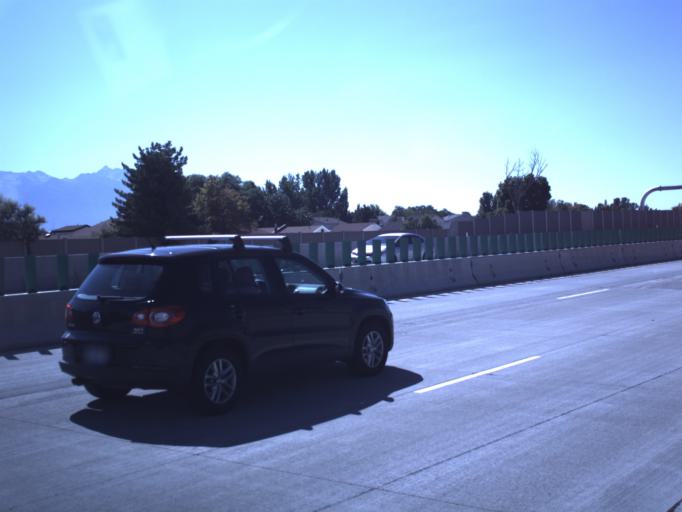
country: US
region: Utah
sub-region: Salt Lake County
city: Taylorsville
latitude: 40.6799
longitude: -111.9521
